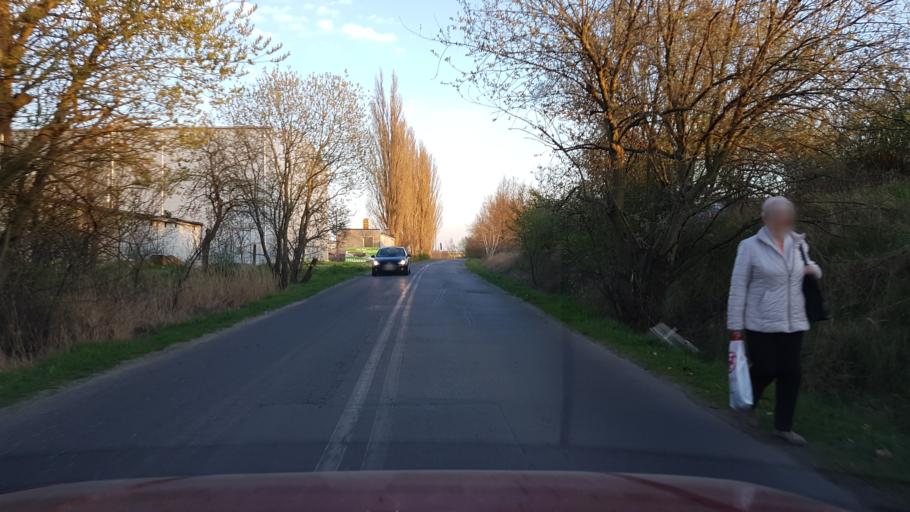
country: PL
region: West Pomeranian Voivodeship
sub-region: Powiat stargardzki
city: Stargard Szczecinski
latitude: 53.3500
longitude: 15.0164
